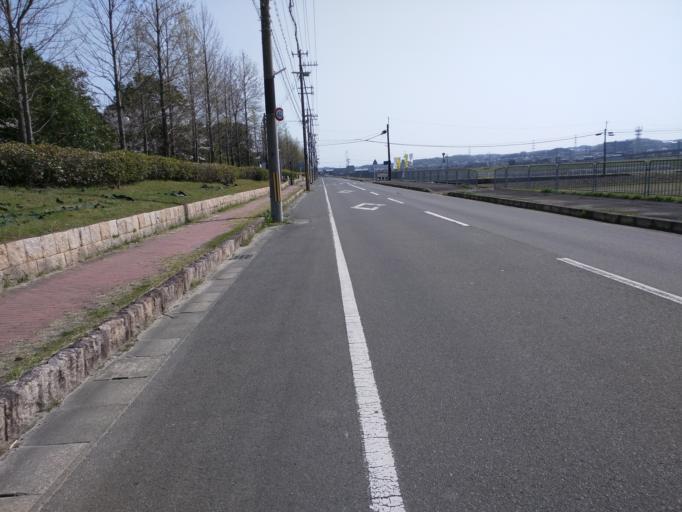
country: JP
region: Kyoto
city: Tanabe
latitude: 34.7753
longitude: 135.7975
